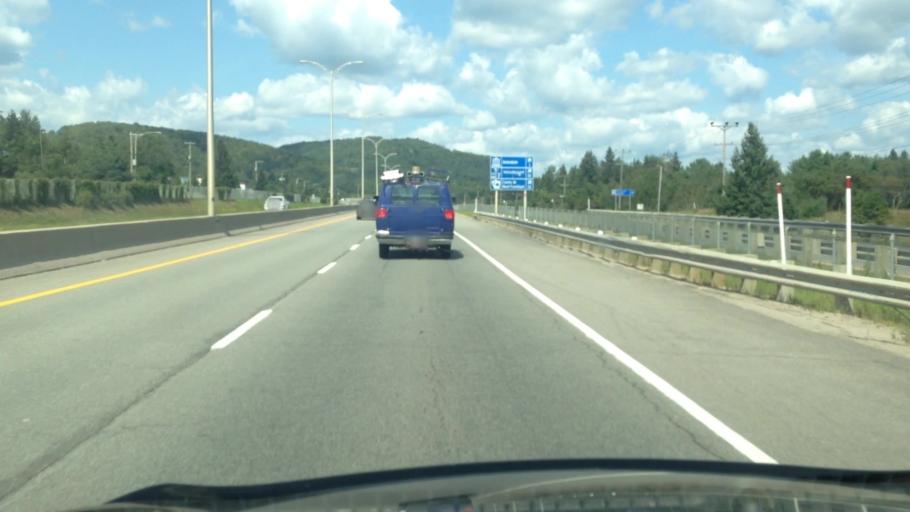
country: CA
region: Quebec
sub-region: Laurentides
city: Mont-Tremblant
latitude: 46.1246
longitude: -74.6083
